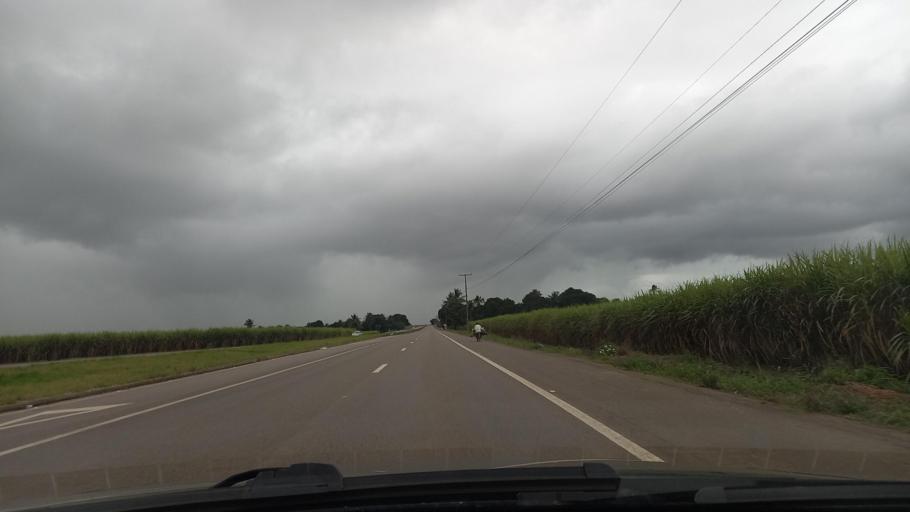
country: BR
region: Alagoas
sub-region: Limoeiro De Anadia
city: Cajueiro
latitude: -9.7628
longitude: -36.4327
